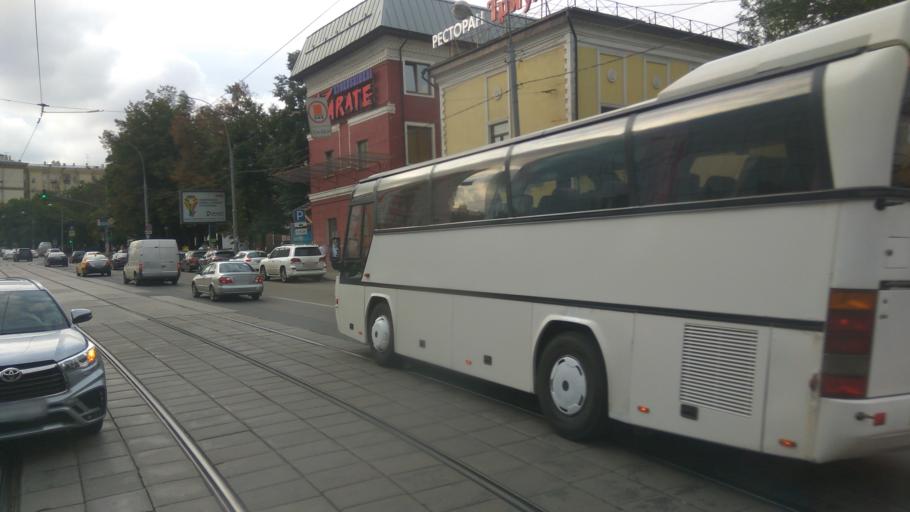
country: RU
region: Moscow
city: Taganskiy
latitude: 55.7541
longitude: 37.6625
